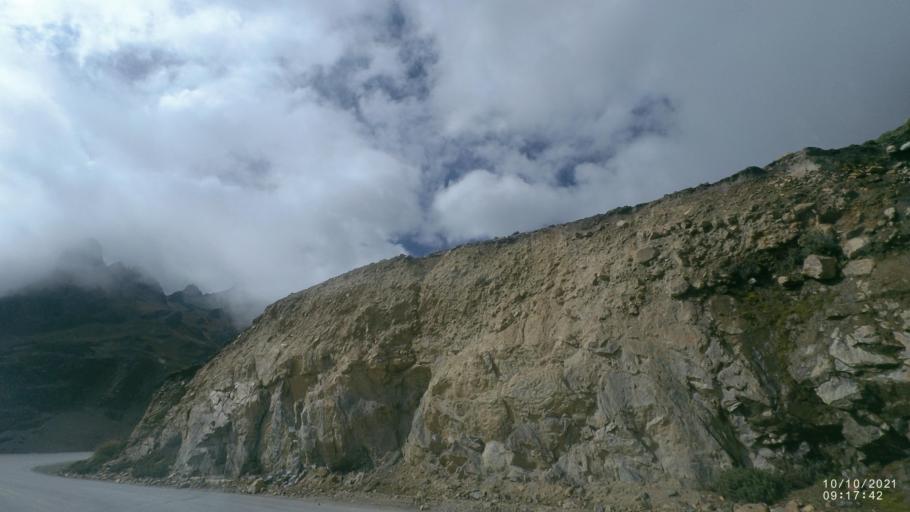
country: BO
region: La Paz
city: Quime
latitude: -17.0480
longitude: -67.2971
